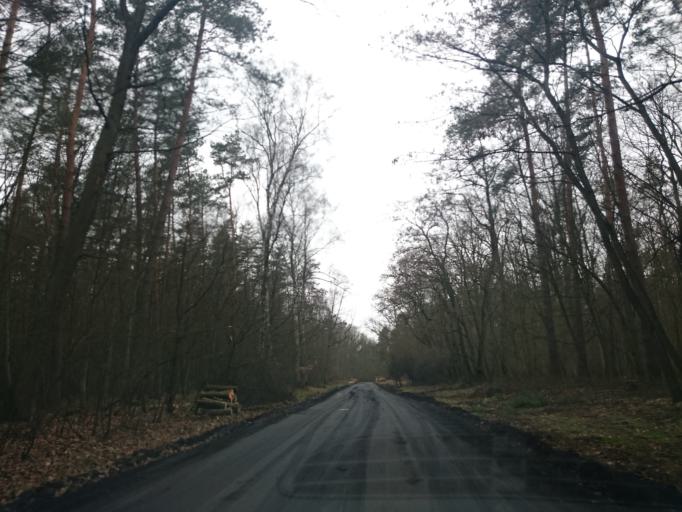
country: PL
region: Kujawsko-Pomorskie
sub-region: Powiat golubsko-dobrzynski
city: Ciechocin
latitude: 53.0733
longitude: 18.8522
